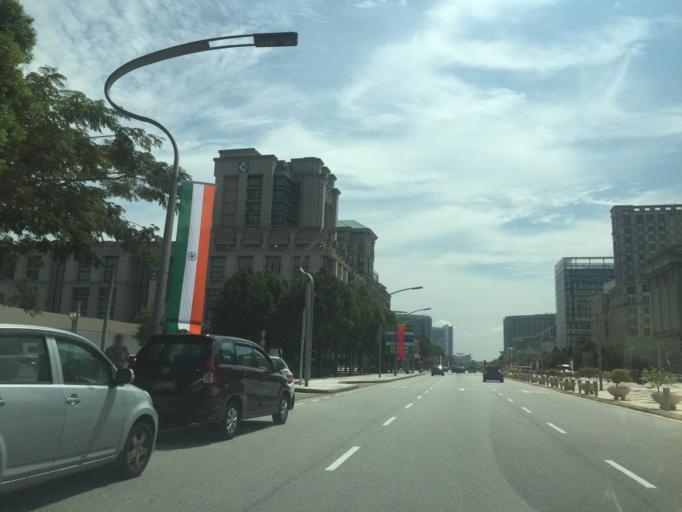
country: MY
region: Putrajaya
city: Putrajaya
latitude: 2.9226
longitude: 101.6869
